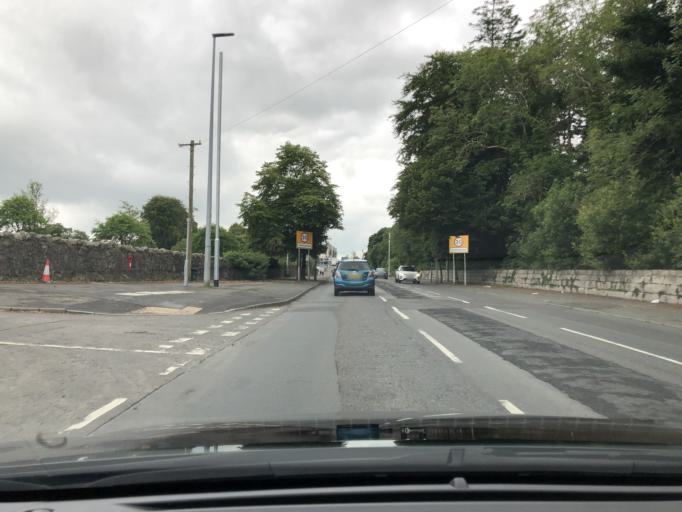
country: GB
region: Northern Ireland
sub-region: Down District
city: Castlewellan
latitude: 54.2594
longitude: -5.9369
